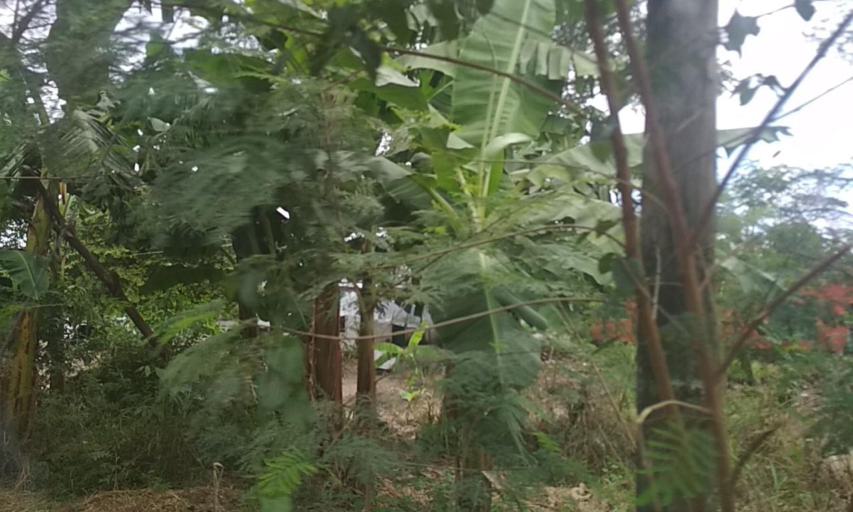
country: MX
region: Veracruz
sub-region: Martinez de la Torre
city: El Progreso
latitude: 20.0943
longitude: -97.0132
